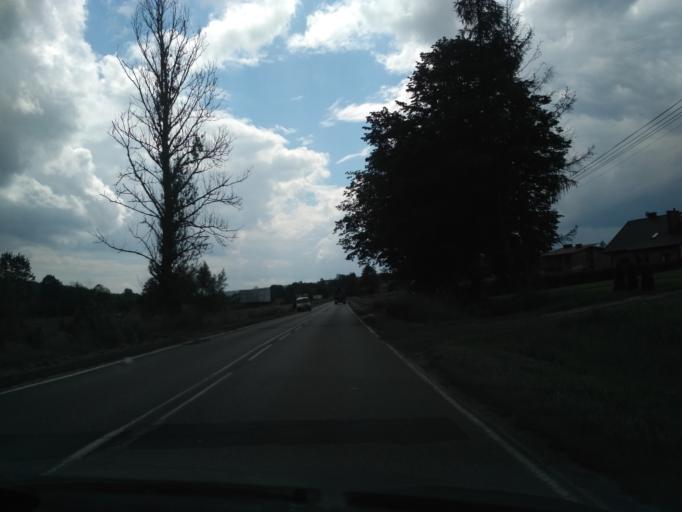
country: PL
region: Subcarpathian Voivodeship
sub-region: Powiat rzeszowski
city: Blazowa
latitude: 49.9367
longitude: 22.1081
